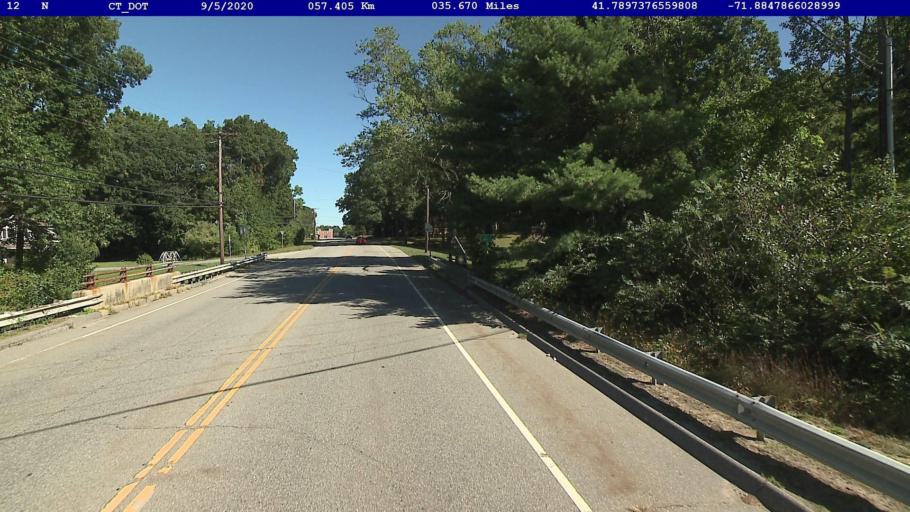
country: US
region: Connecticut
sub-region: Windham County
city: Danielson
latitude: 41.7897
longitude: -71.8848
